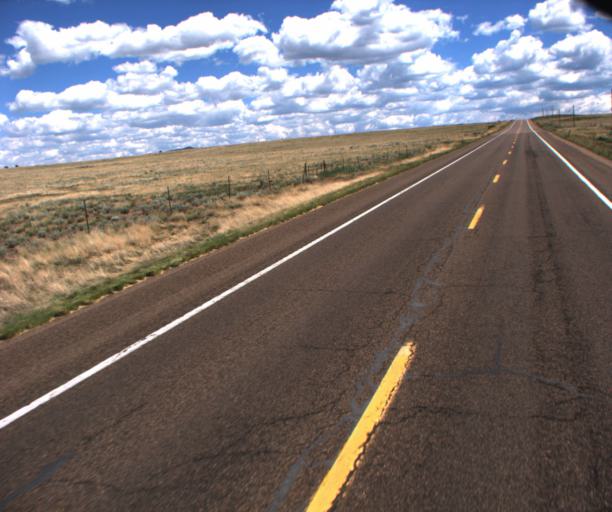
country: US
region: Arizona
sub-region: Apache County
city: Springerville
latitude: 34.1849
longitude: -109.3326
